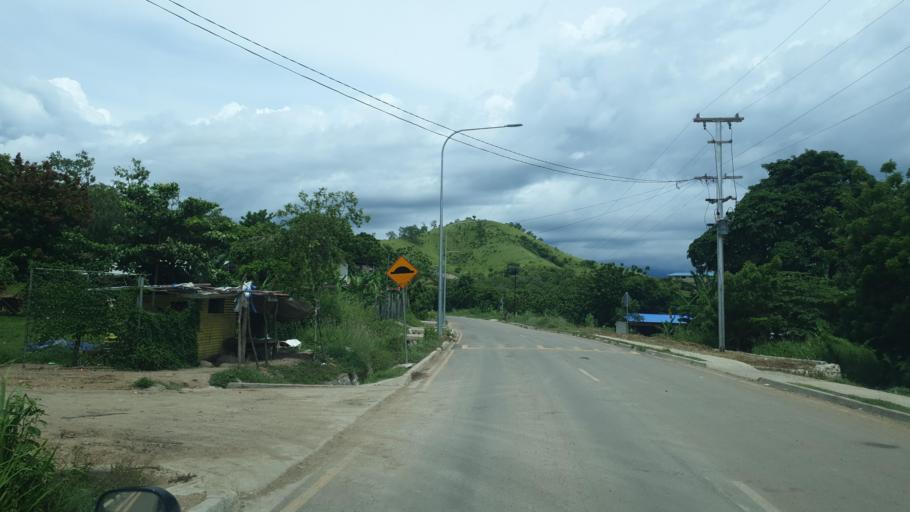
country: PG
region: National Capital
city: Port Moresby
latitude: -9.5287
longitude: 147.2460
